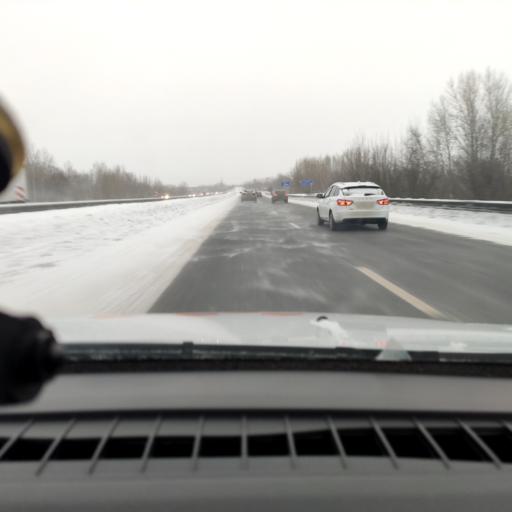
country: RU
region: Samara
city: Kinel'
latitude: 53.2552
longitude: 50.5827
